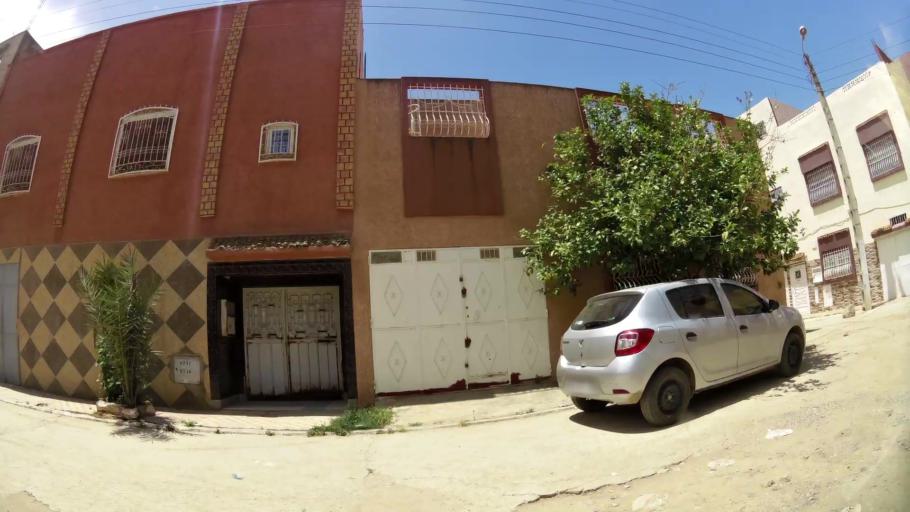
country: MA
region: Rabat-Sale-Zemmour-Zaer
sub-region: Khemisset
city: Khemisset
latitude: 33.8250
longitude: -6.0804
